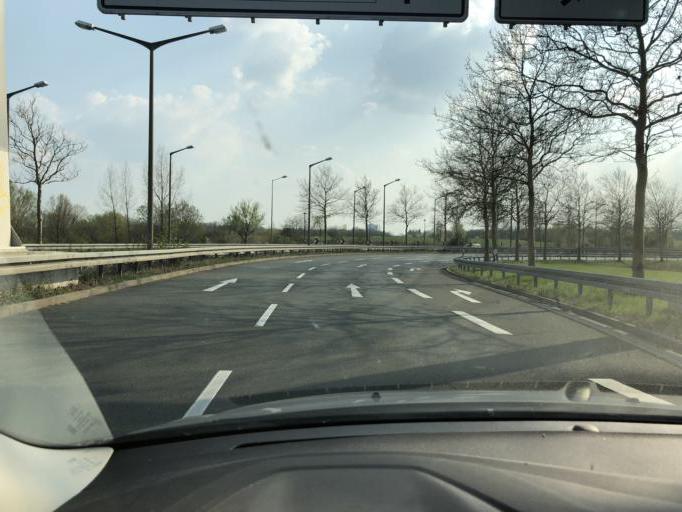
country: DE
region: Saxony
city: Rackwitz
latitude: 51.3931
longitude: 12.4205
